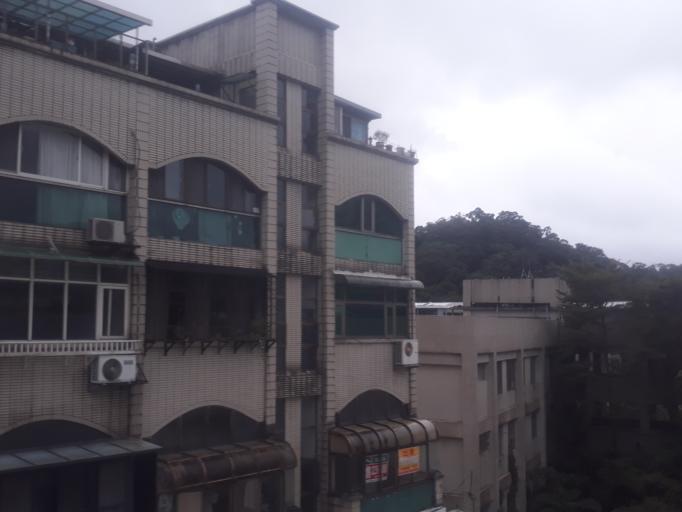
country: TW
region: Taipei
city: Taipei
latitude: 25.0031
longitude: 121.5573
